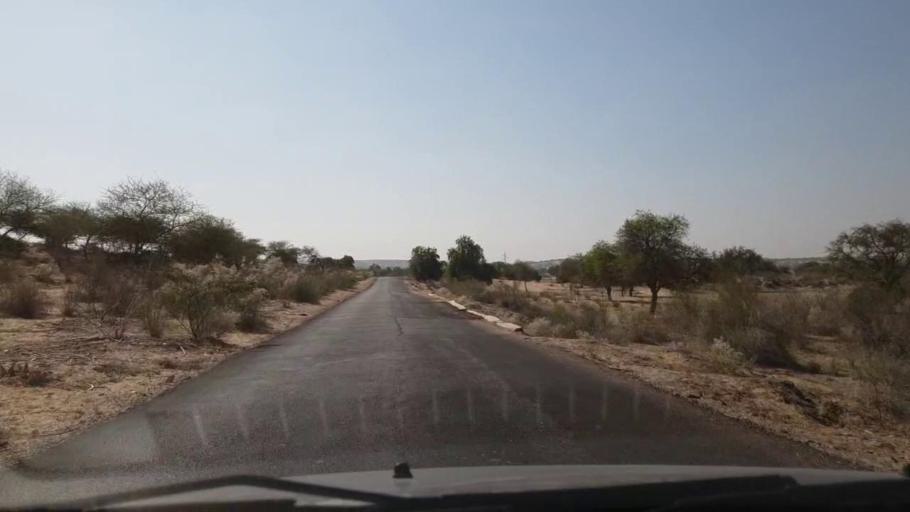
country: PK
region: Sindh
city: Mithi
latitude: 24.6671
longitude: 69.7631
